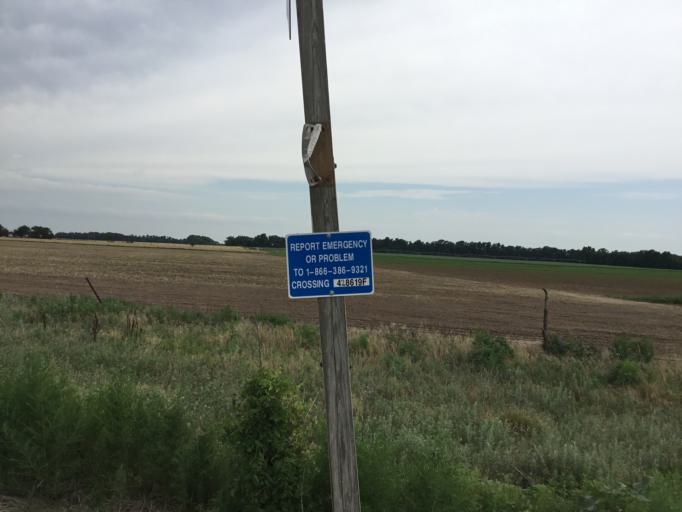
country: US
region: Kansas
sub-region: Sedgwick County
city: Cheney
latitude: 37.4447
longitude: -97.8297
